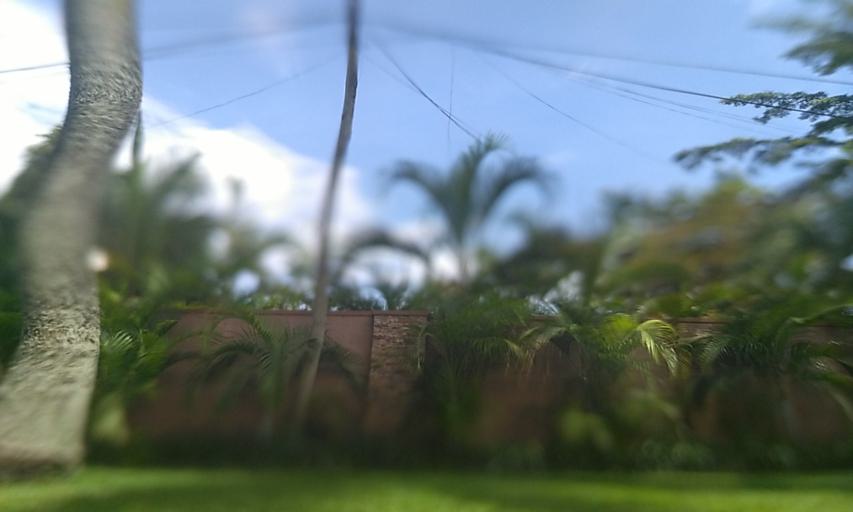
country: UG
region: Central Region
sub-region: Kampala District
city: Kampala
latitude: 0.3357
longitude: 32.5957
